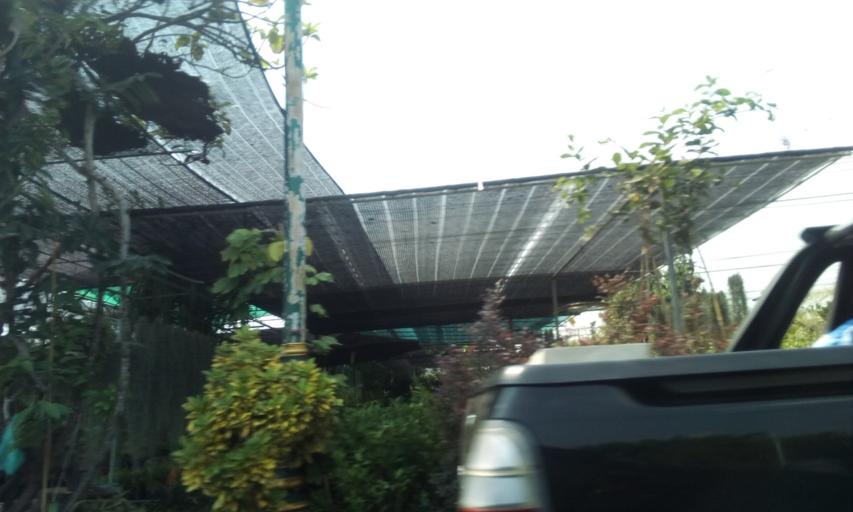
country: TH
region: Nakhon Nayok
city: Ongkharak
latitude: 14.1065
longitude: 100.9436
